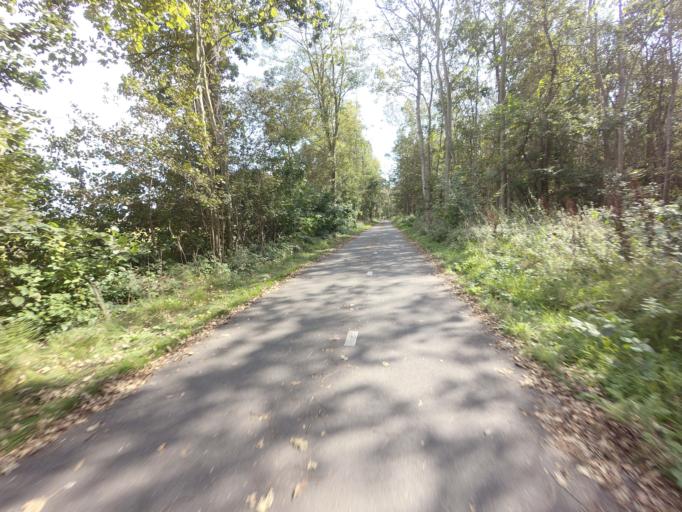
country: NL
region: Zeeland
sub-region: Gemeente Vlissingen
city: Vlissingen
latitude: 51.4811
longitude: 3.5182
